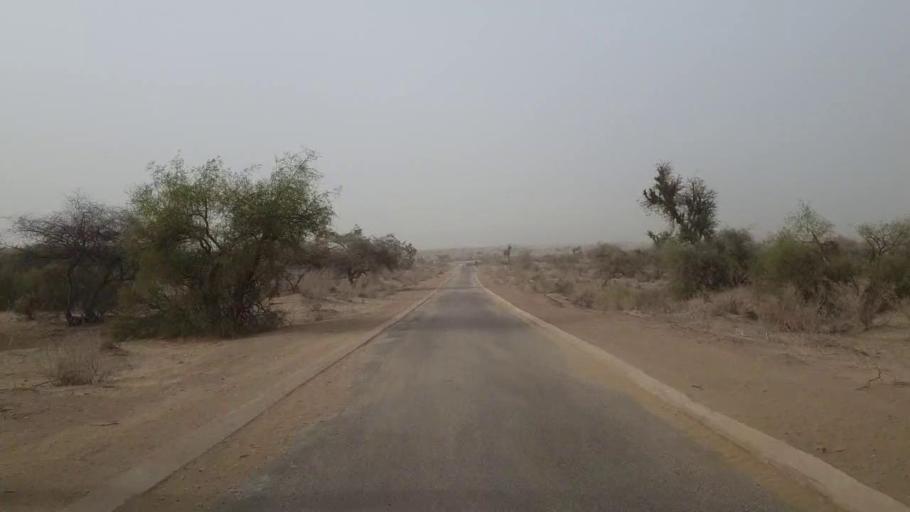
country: PK
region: Sindh
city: Islamkot
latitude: 24.5682
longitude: 70.3636
